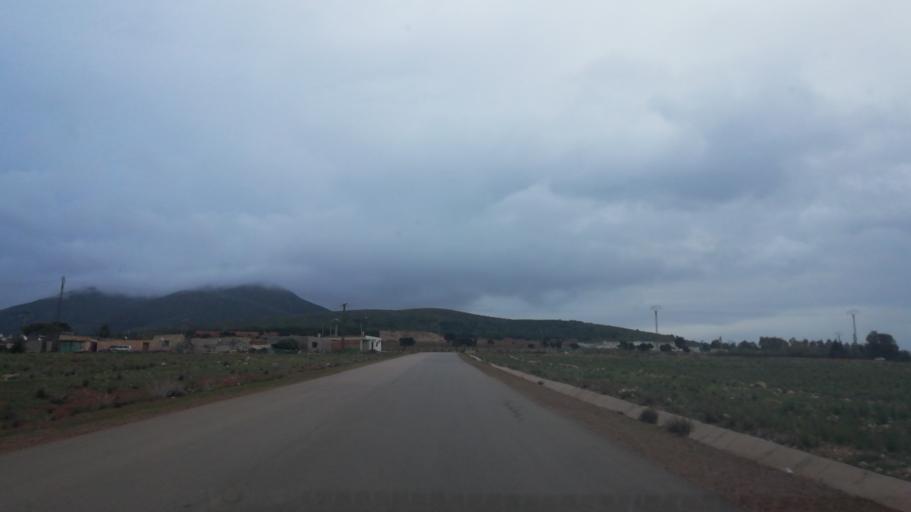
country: DZ
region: Oran
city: Bir el Djir
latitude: 35.7607
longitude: -0.5286
